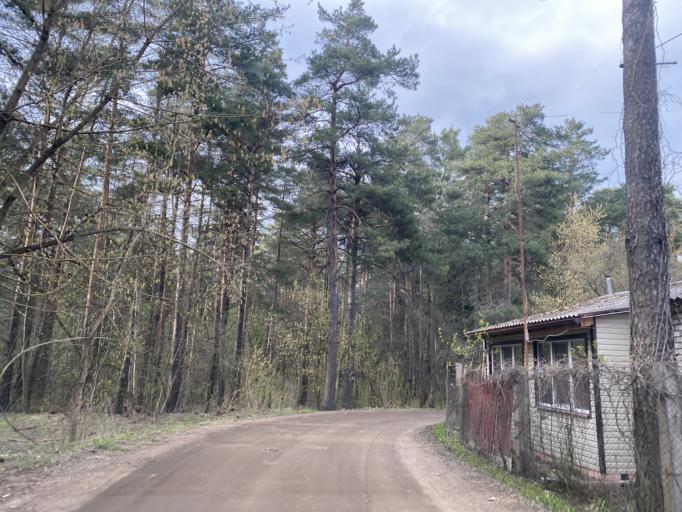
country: BY
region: Minsk
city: Vyaliki Trastsyanets
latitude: 53.9155
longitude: 27.6624
